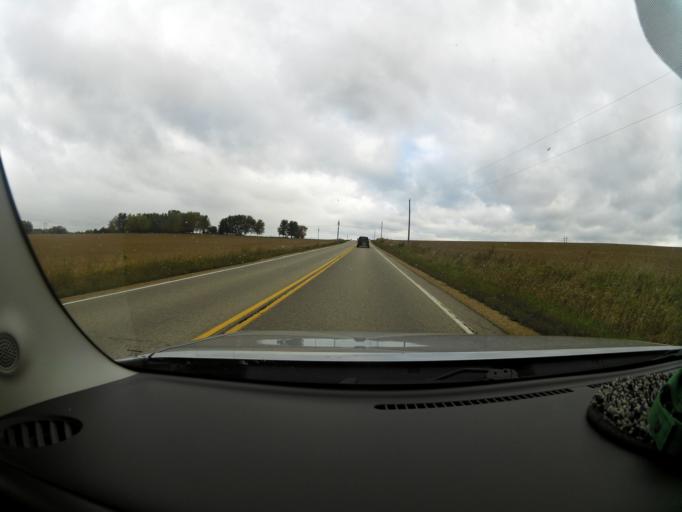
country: US
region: Minnesota
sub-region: Washington County
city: Afton
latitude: 44.8812
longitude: -92.8625
